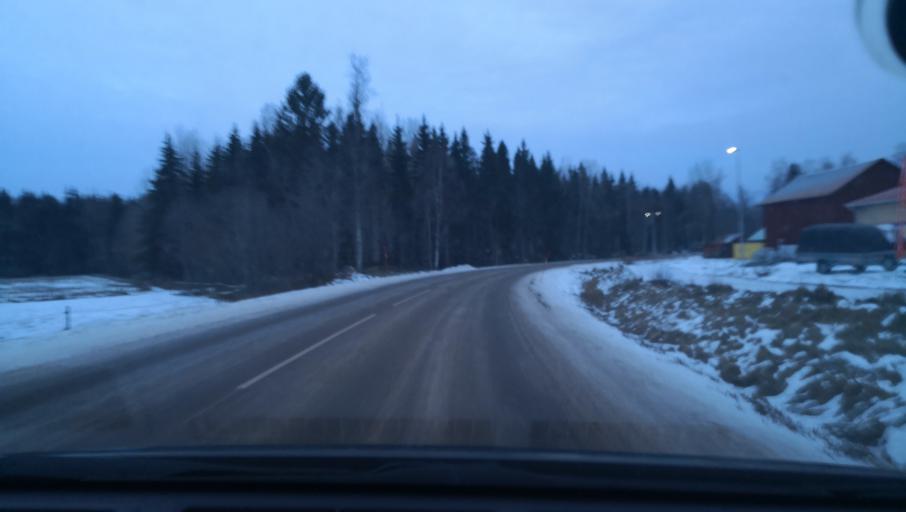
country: SE
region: Dalarna
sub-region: Avesta Kommun
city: Horndal
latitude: 60.1990
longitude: 16.4615
